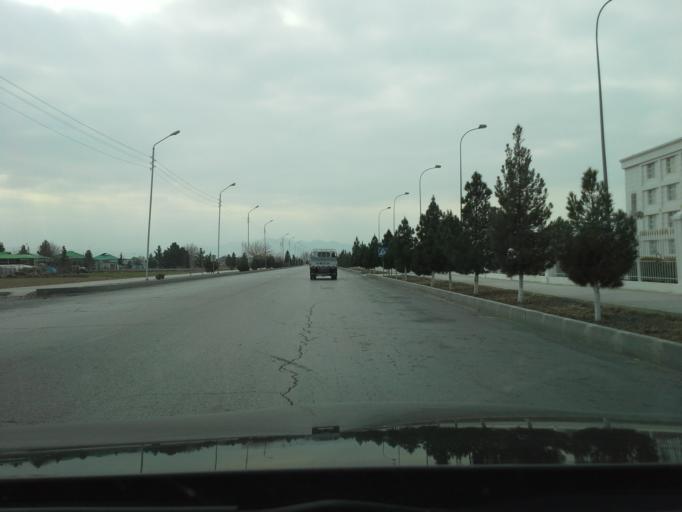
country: TM
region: Ahal
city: Abadan
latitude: 38.0352
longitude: 58.2705
